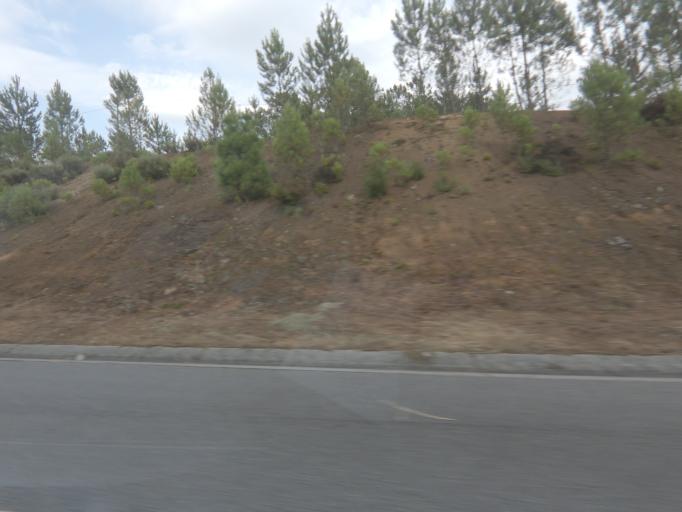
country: PT
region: Viseu
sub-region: Viseu
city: Campo
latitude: 40.7546
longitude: -7.9219
